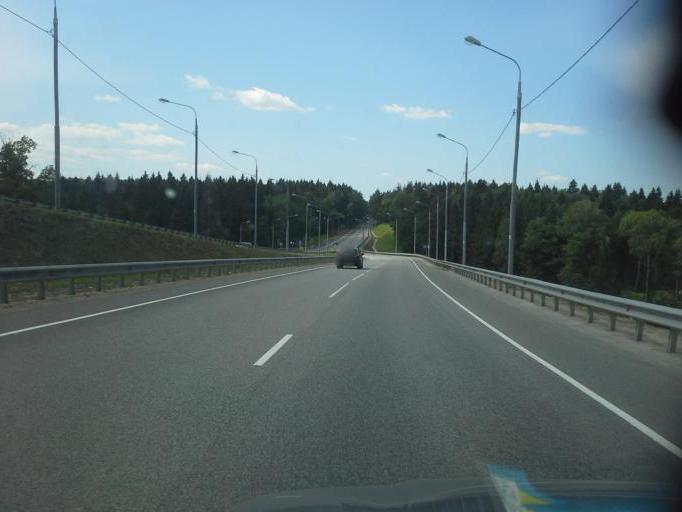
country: RU
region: Moskovskaya
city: Odintsovo
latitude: 55.6898
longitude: 37.2450
